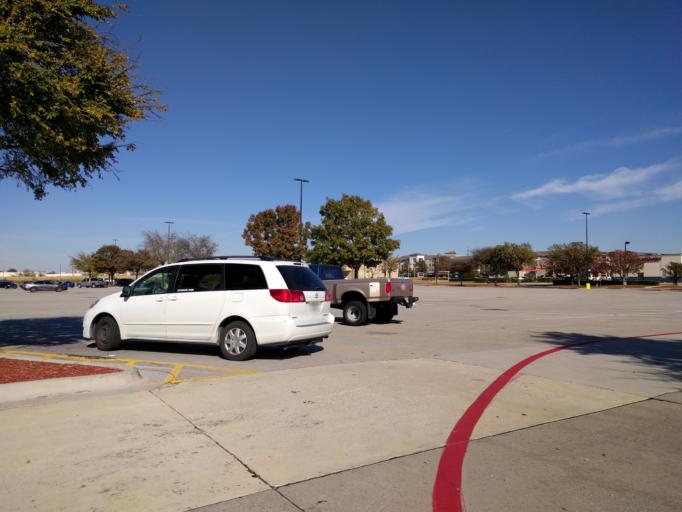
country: US
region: Texas
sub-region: Dallas County
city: Richardson
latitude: 33.0036
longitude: -96.7699
